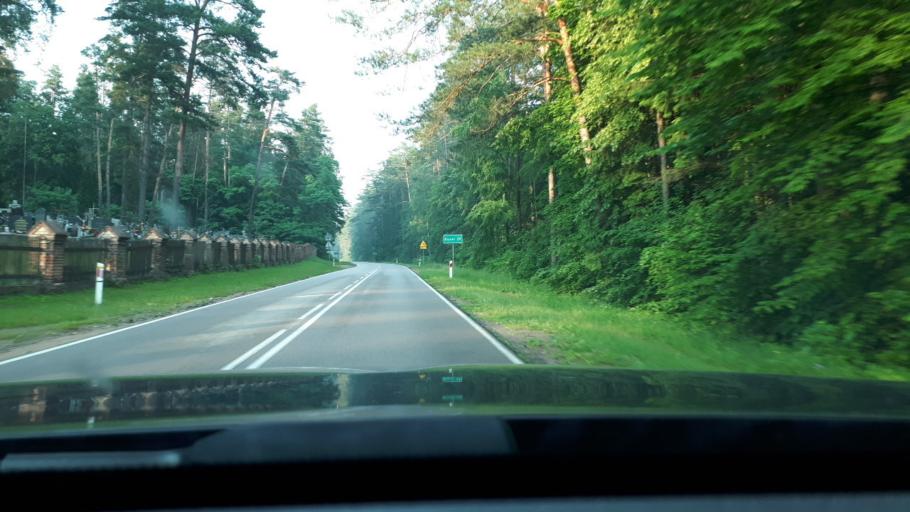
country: PL
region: Podlasie
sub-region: Powiat bialostocki
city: Suprasl
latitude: 53.2198
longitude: 23.3486
